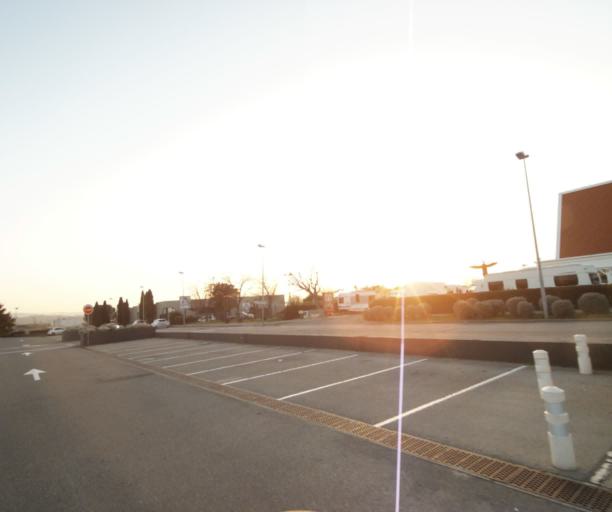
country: FR
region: Provence-Alpes-Cote d'Azur
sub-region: Departement des Bouches-du-Rhone
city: Saint-Victoret
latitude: 43.4254
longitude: 5.2699
